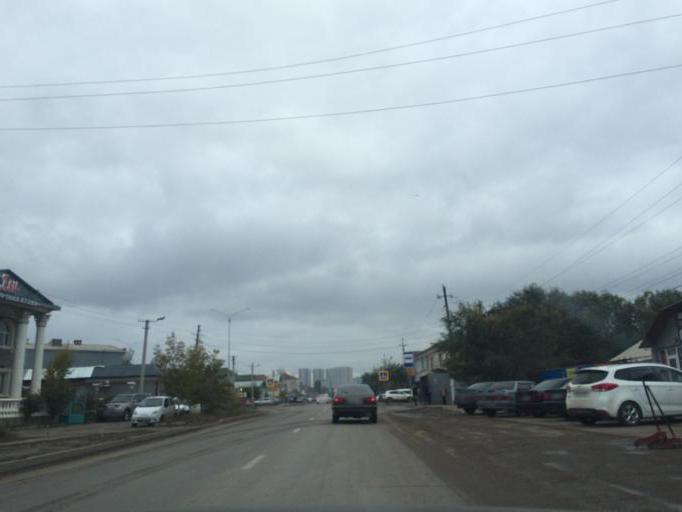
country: KZ
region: Astana Qalasy
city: Astana
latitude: 51.1355
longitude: 71.4990
